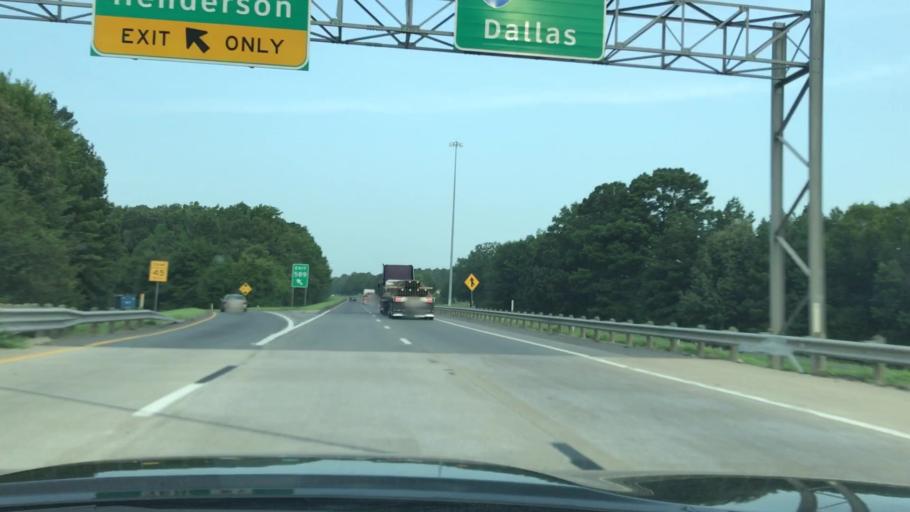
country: US
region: Texas
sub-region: Gregg County
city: Kilgore
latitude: 32.4354
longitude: -94.8277
